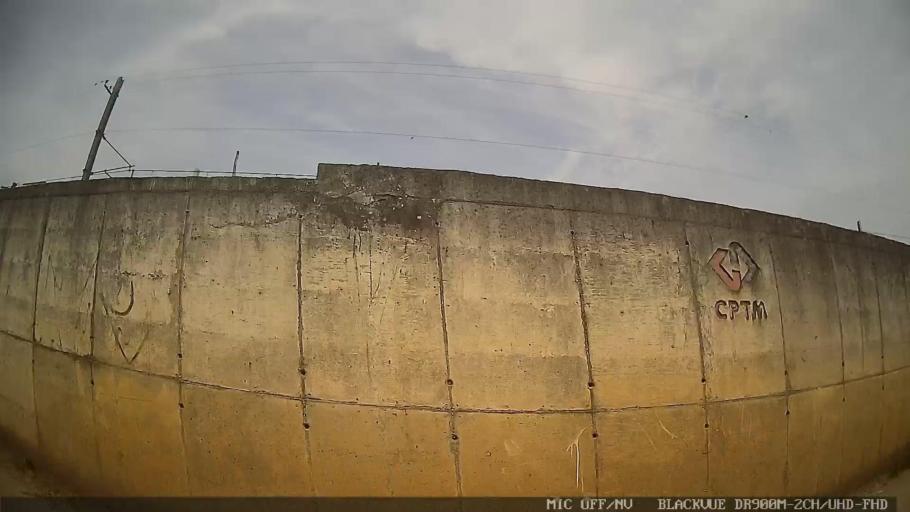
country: BR
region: Sao Paulo
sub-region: Itaquaquecetuba
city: Itaquaquecetuba
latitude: -23.4930
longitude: -46.3372
